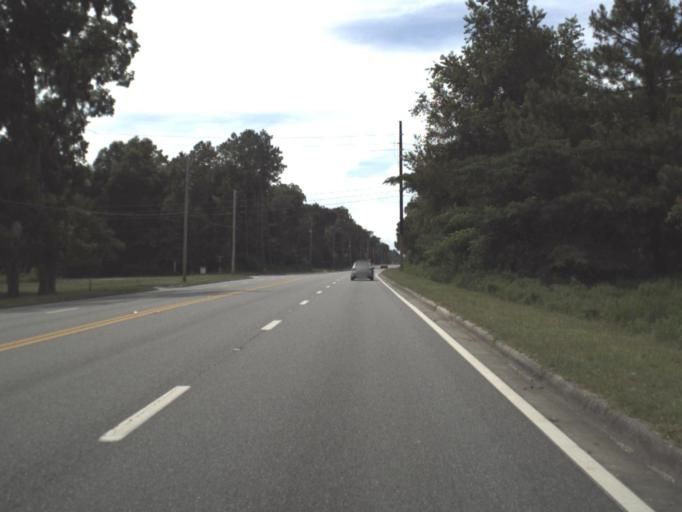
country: US
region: Florida
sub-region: Taylor County
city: Perry
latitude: 30.0950
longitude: -83.5447
